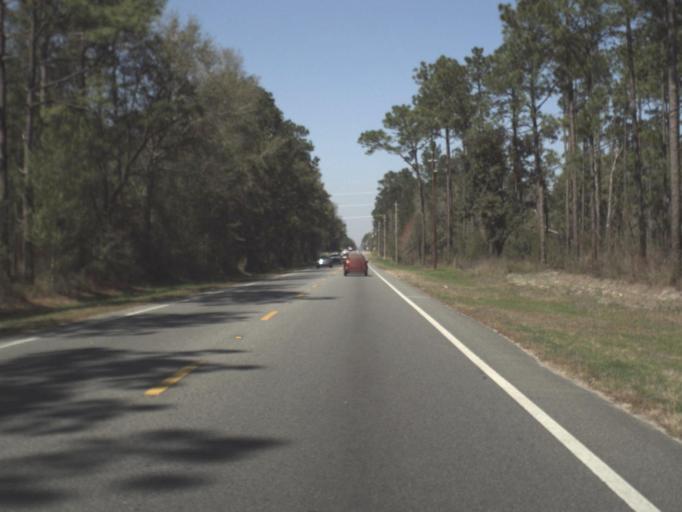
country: US
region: Florida
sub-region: Leon County
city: Woodville
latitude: 30.3444
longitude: -84.2564
